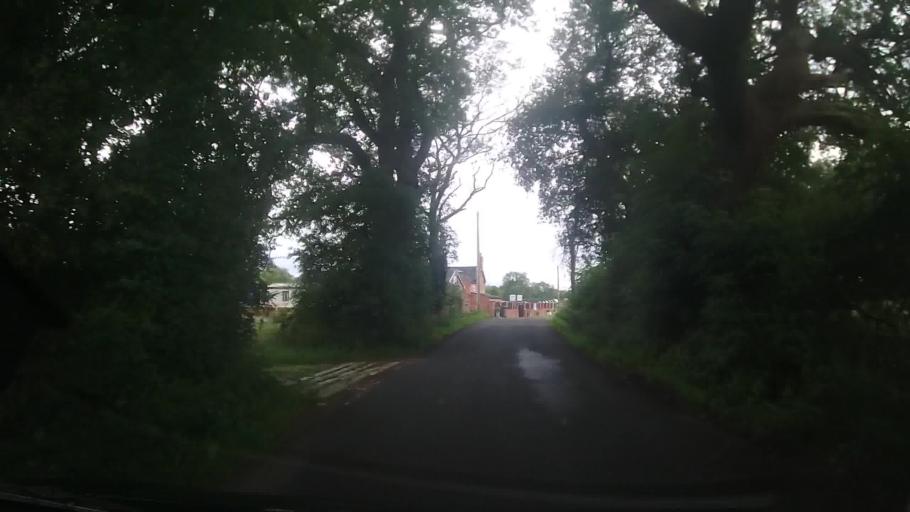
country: GB
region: England
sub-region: Shropshire
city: Whitchurch
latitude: 52.9259
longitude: -2.7296
